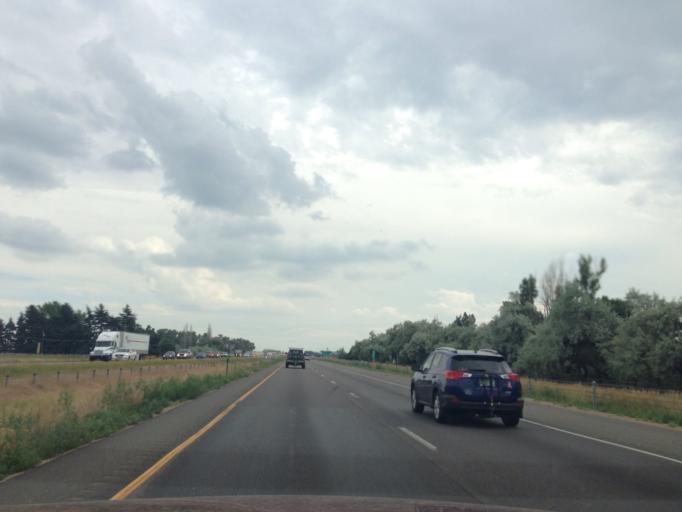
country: US
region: Colorado
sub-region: Weld County
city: Windsor
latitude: 40.4698
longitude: -104.9920
